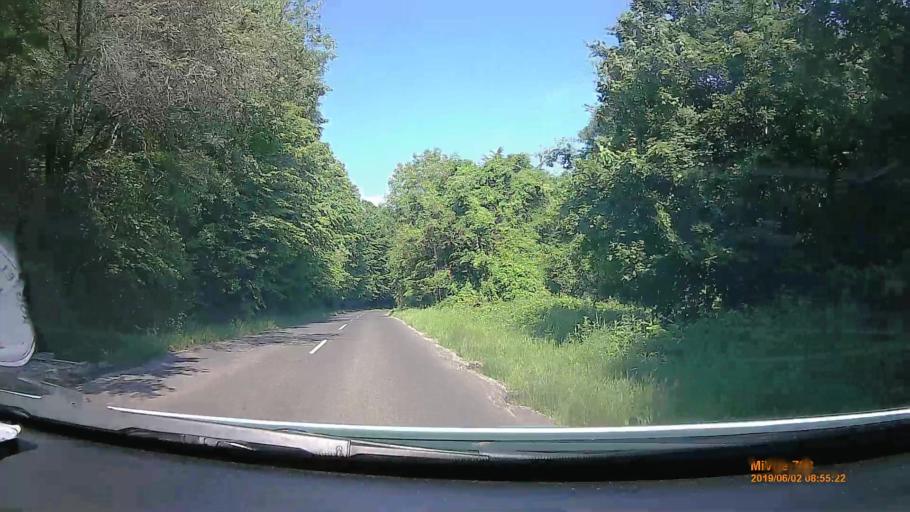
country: HU
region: Borsod-Abauj-Zemplen
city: Sajobabony
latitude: 48.1538
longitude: 20.6625
